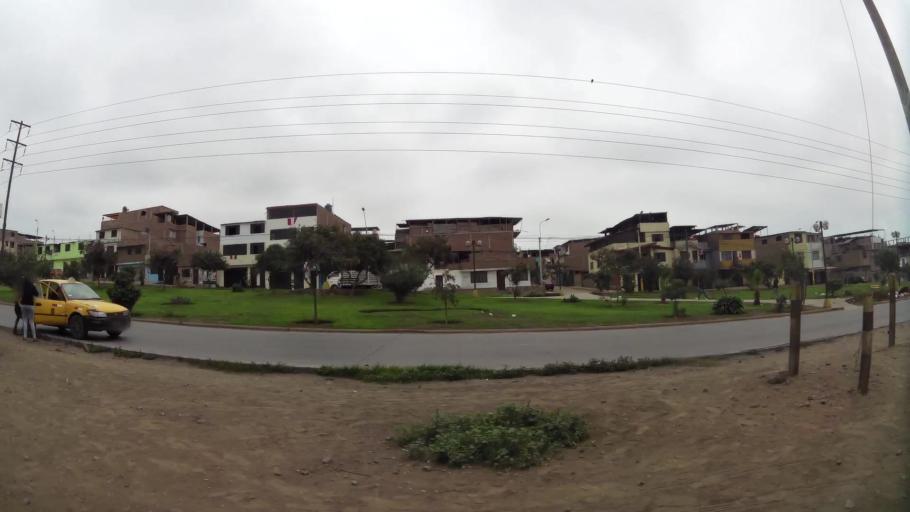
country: PE
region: Lima
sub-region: Lima
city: Surco
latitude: -12.1948
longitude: -76.9522
